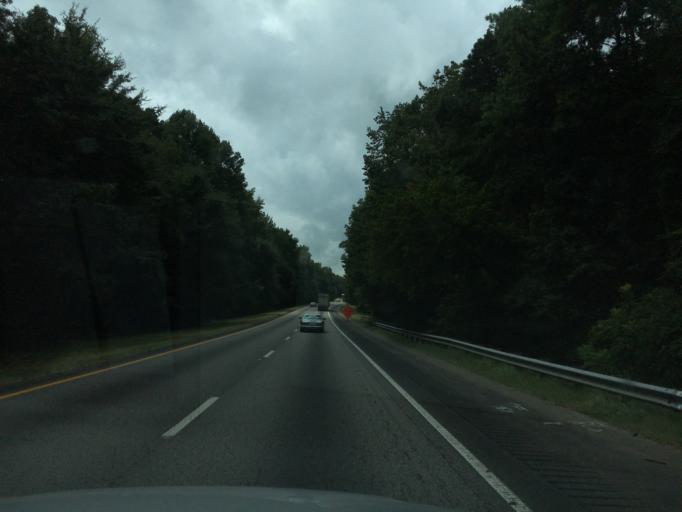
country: US
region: Georgia
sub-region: Jackson County
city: Braselton
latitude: 34.1348
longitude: -83.6768
